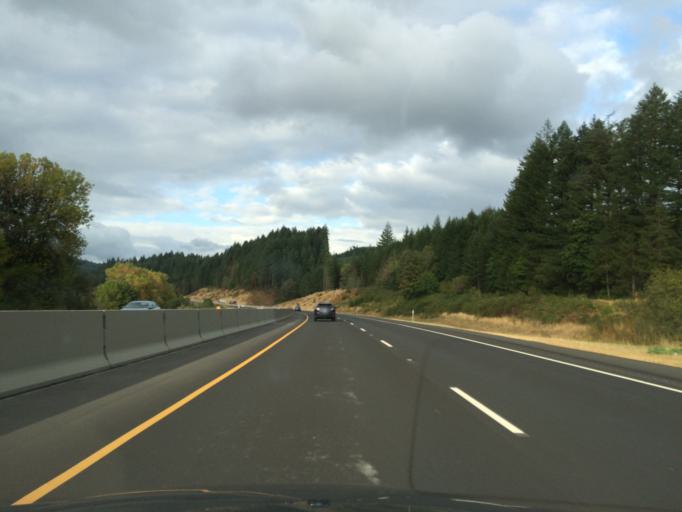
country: US
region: Oregon
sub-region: Lane County
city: Cottage Grove
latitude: 43.7366
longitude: -123.1905
